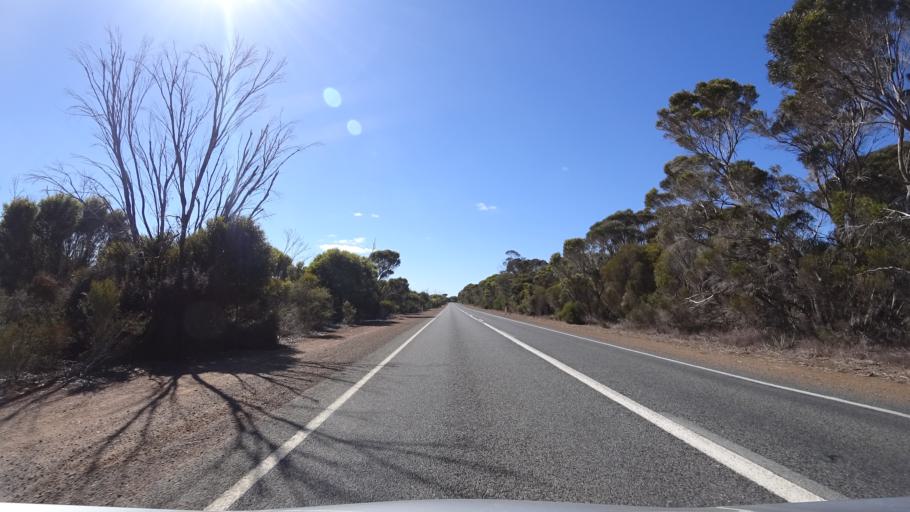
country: AU
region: South Australia
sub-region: Kangaroo Island
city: Kingscote
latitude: -35.7283
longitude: 137.5627
